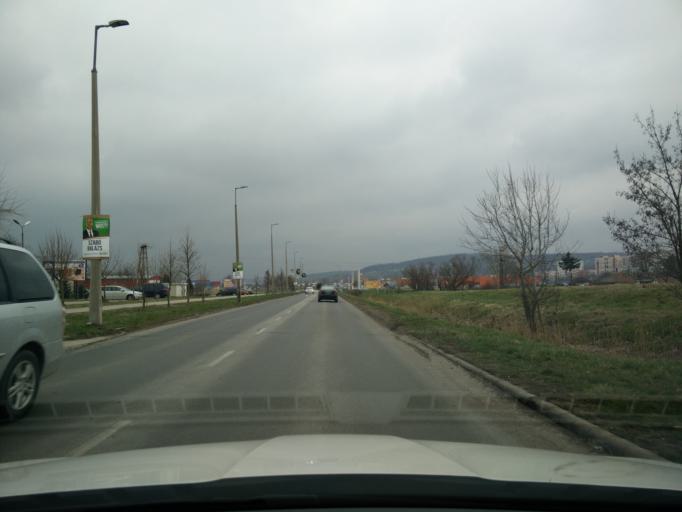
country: HU
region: Tolna
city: Szekszard
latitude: 46.3364
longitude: 18.7075
